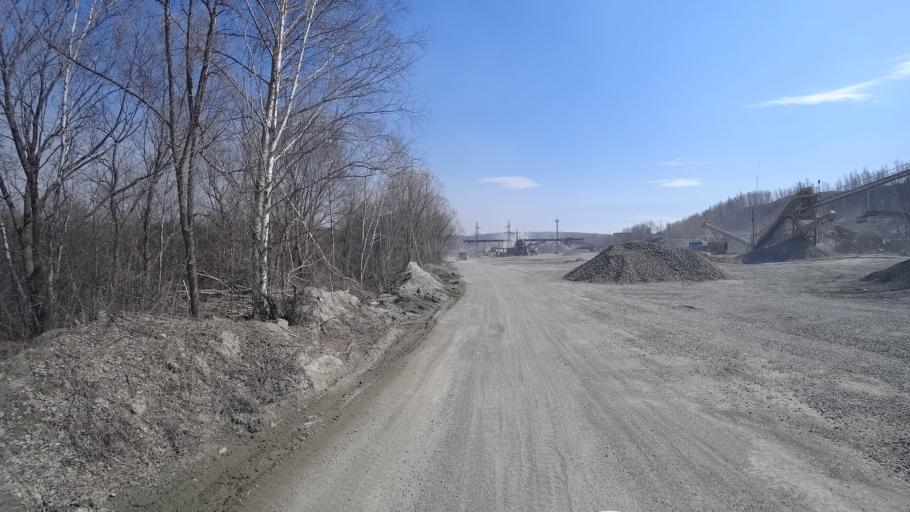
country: RU
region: Amur
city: Novobureyskiy
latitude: 49.7950
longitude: 129.9576
